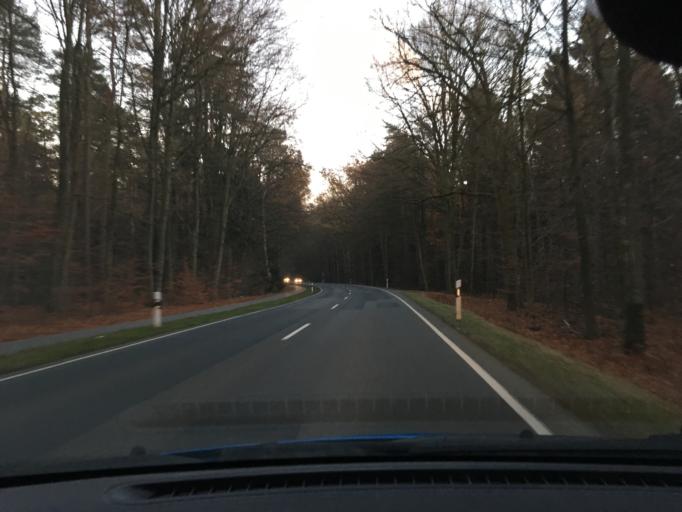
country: DE
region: Lower Saxony
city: Uelzen
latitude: 52.9837
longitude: 10.5196
